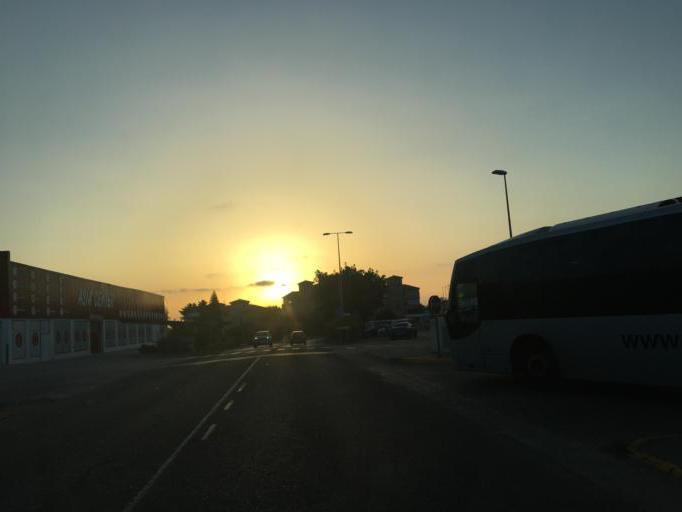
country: ES
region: Murcia
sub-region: Murcia
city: La Manga del Mar Menor
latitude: 37.6282
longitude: -0.7088
